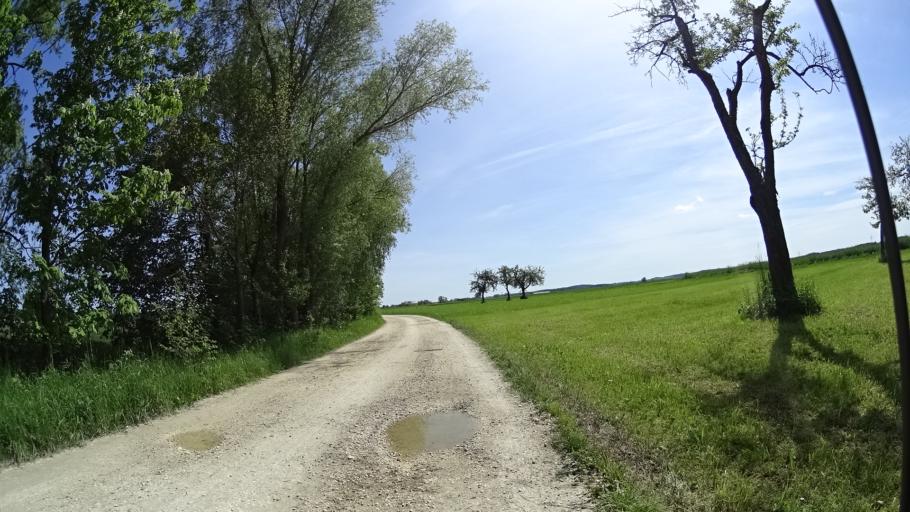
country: DE
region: Bavaria
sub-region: Swabia
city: Pfaffenhofen an der Roth
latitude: 48.3370
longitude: 10.1563
